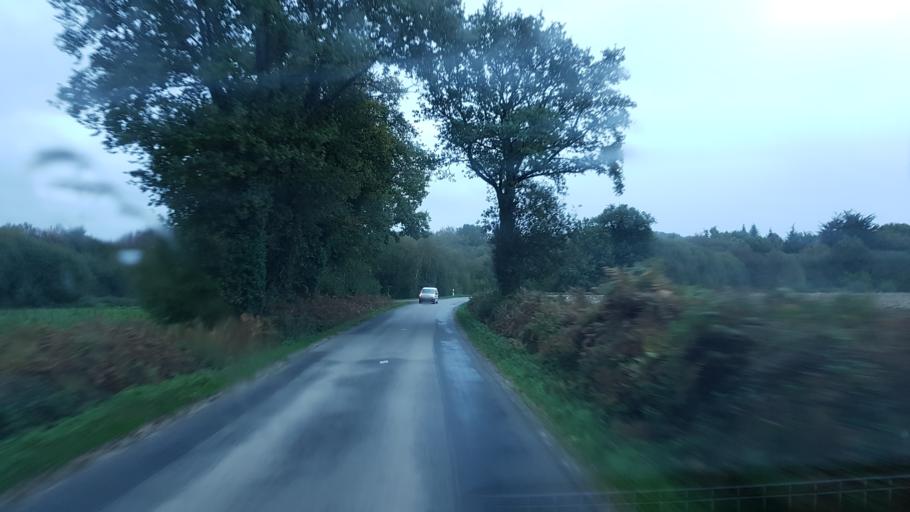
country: FR
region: Brittany
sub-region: Departement du Morbihan
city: Sulniac
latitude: 47.6849
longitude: -2.5716
